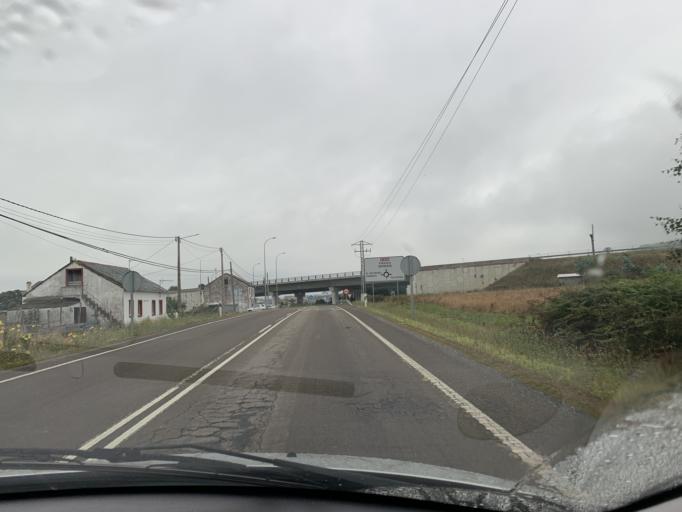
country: ES
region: Galicia
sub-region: Provincia de Lugo
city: Ribadeo
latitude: 43.5435
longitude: -7.0784
